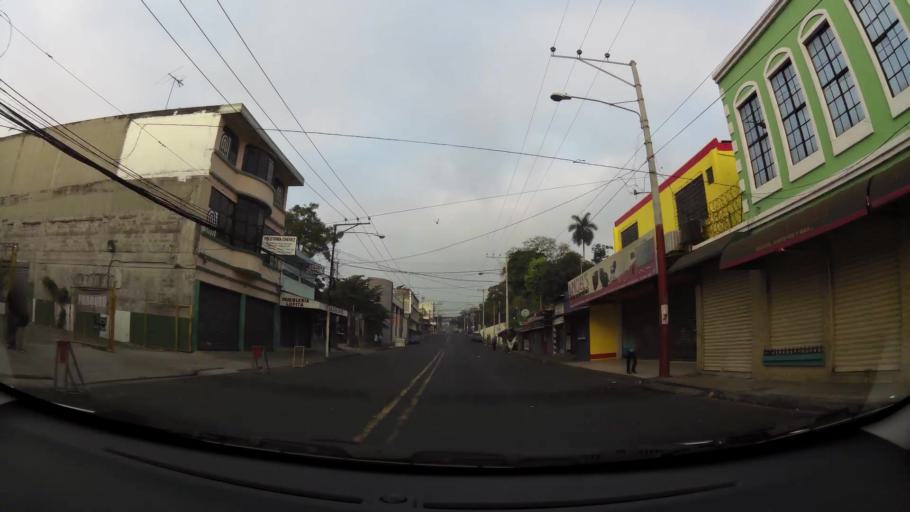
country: SV
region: San Salvador
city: San Salvador
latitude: 13.6979
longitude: -89.1976
